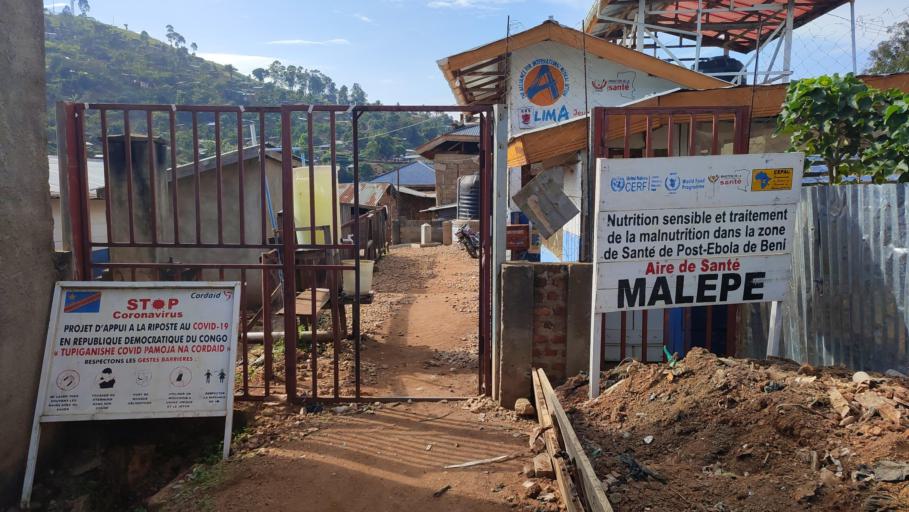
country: CD
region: Nord Kivu
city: Beni
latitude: 0.4872
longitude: 29.4773
